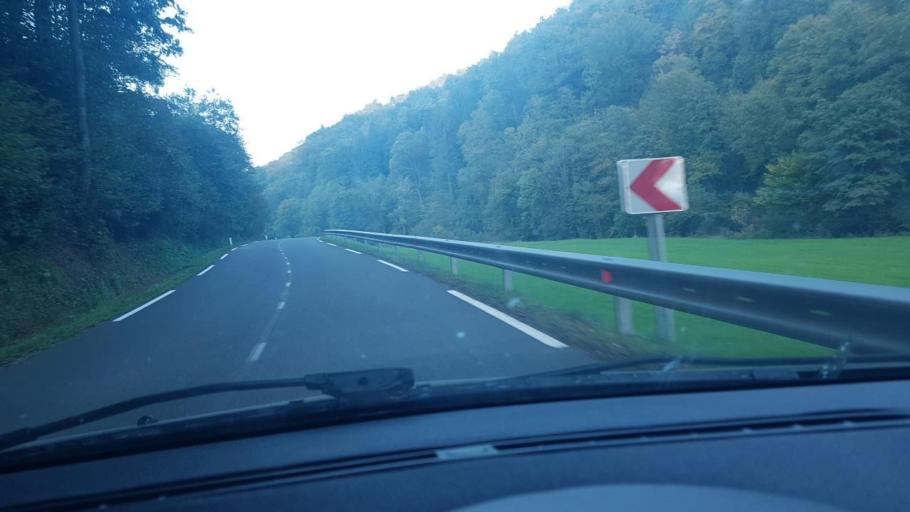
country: SI
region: Majsperk
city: Majsperk
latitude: 46.3107
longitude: 15.7192
